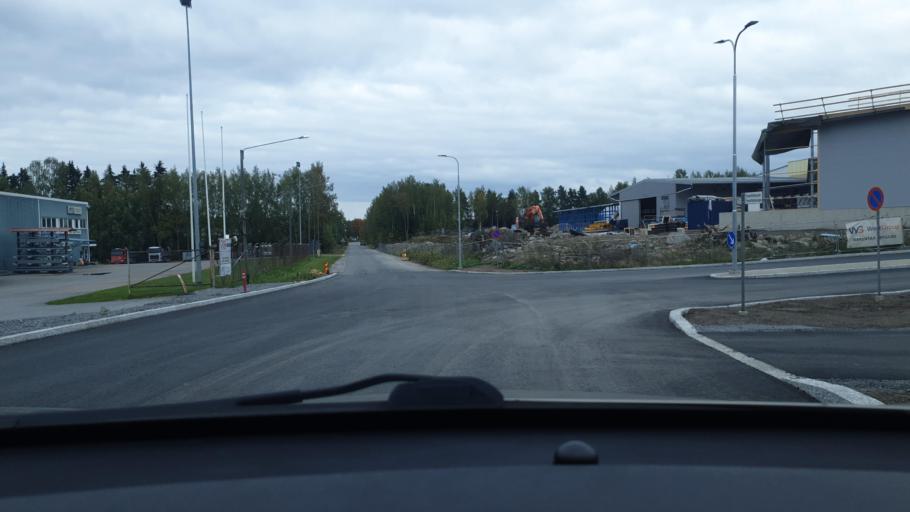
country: FI
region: Ostrobothnia
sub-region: Vaasa
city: Teeriniemi
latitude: 63.0740
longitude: 21.6987
